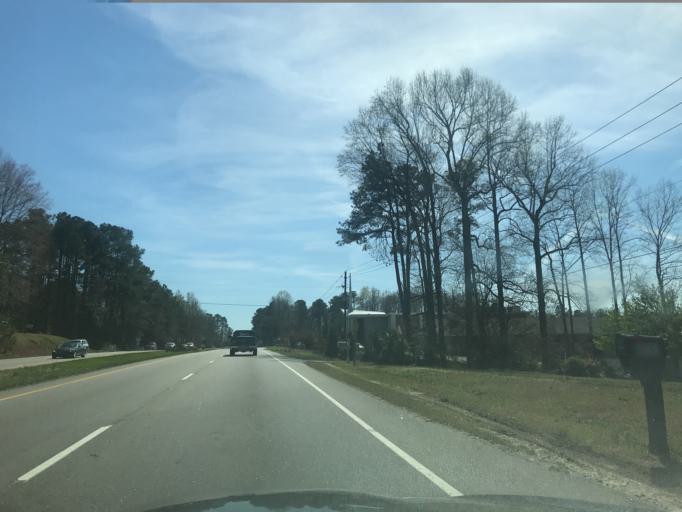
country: US
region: North Carolina
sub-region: Wake County
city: Garner
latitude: 35.6833
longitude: -78.6856
